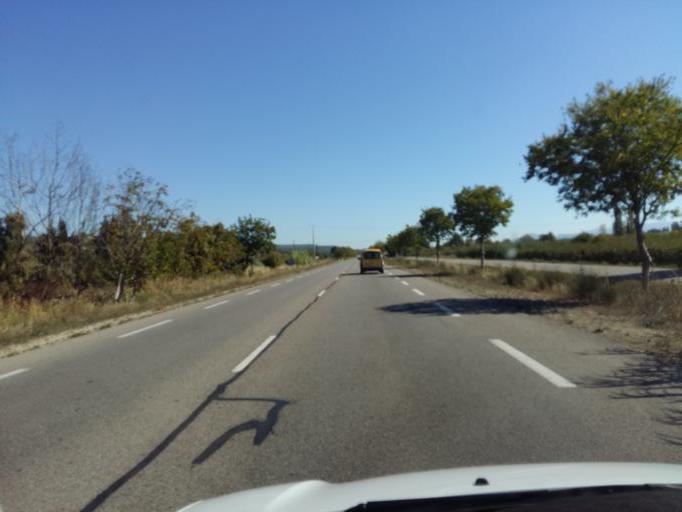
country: FR
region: Provence-Alpes-Cote d'Azur
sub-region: Departement du Vaucluse
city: Cadenet
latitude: 43.7346
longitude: 5.3488
